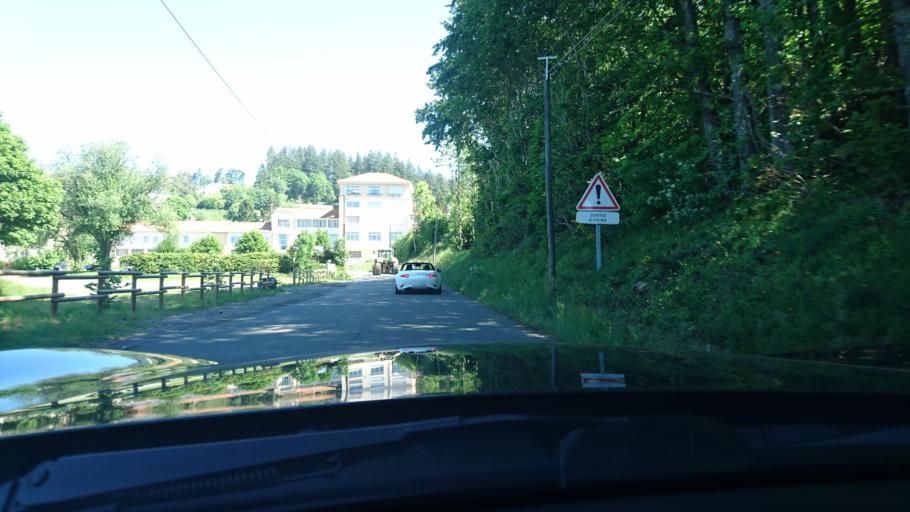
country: FR
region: Rhone-Alpes
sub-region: Departement de la Loire
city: Violay
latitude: 45.8516
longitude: 4.3610
